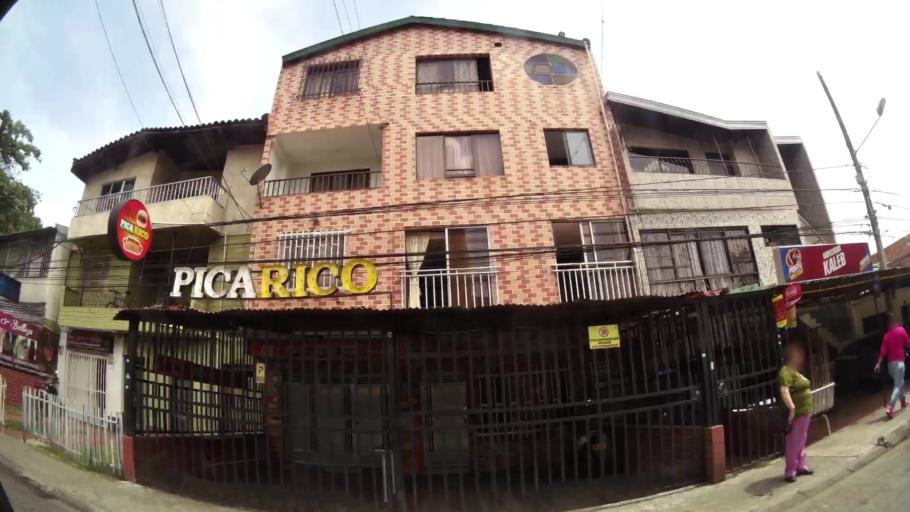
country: CO
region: Antioquia
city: Bello
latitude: 6.3389
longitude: -75.5497
